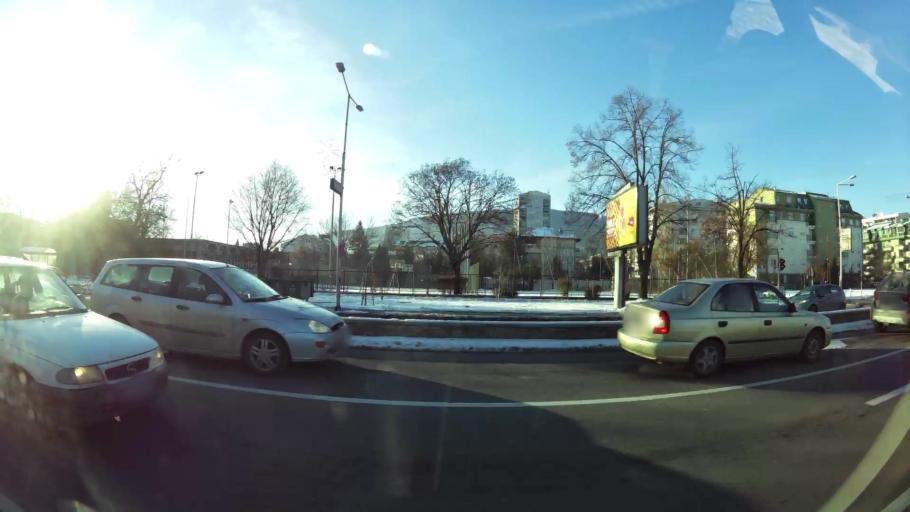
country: MK
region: Karpos
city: Skopje
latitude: 42.0068
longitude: 21.4117
